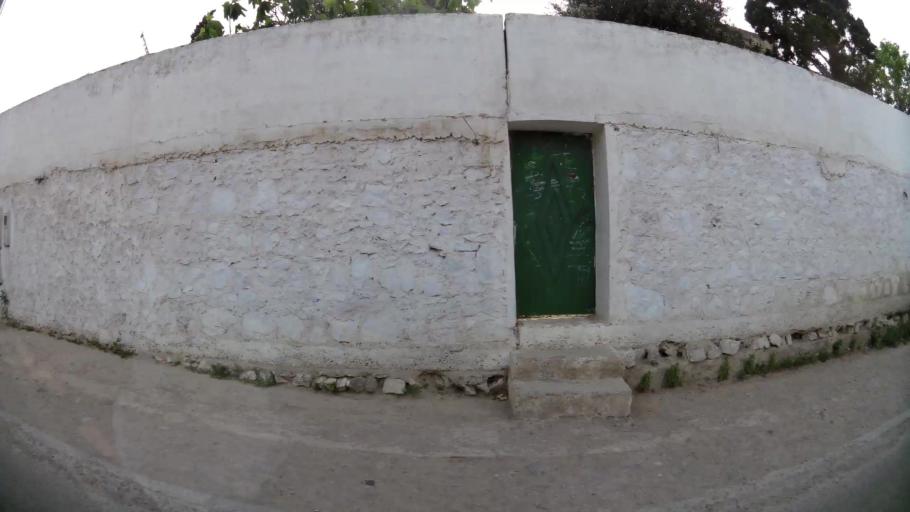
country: MA
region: Tanger-Tetouan
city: Tetouan
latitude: 35.5642
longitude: -5.3962
